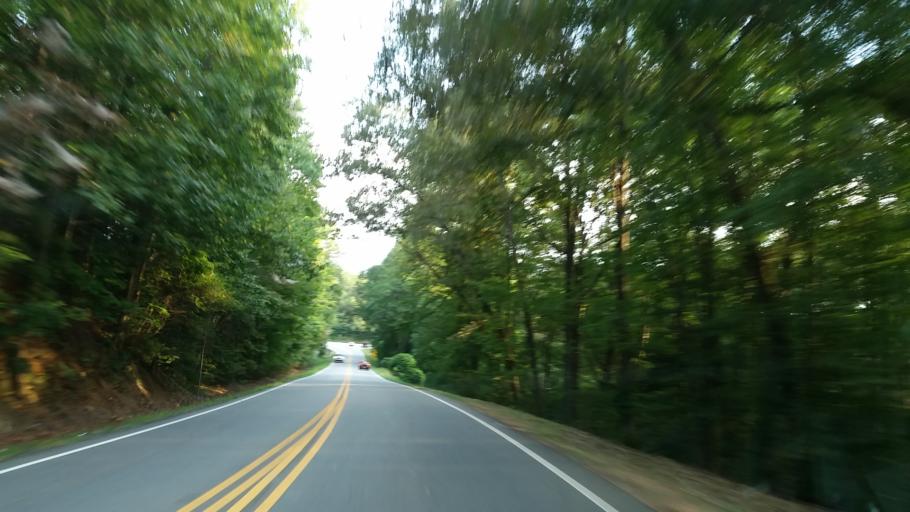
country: US
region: Georgia
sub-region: Lumpkin County
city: Dahlonega
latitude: 34.5529
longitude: -83.9959
